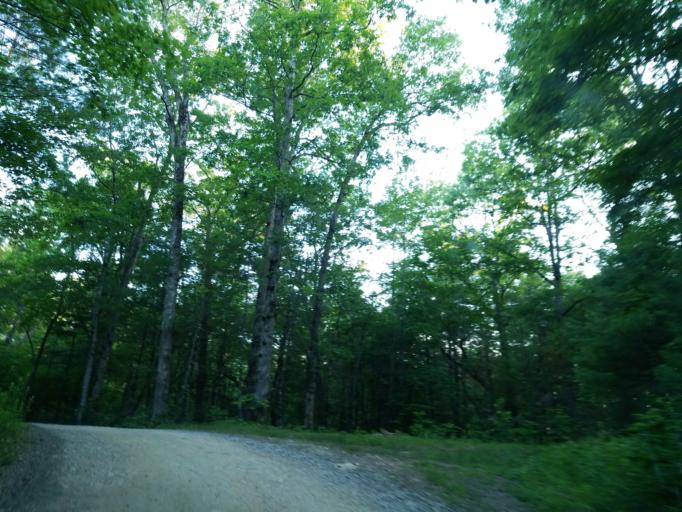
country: US
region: Georgia
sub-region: Fannin County
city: Blue Ridge
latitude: 34.7483
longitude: -84.1779
